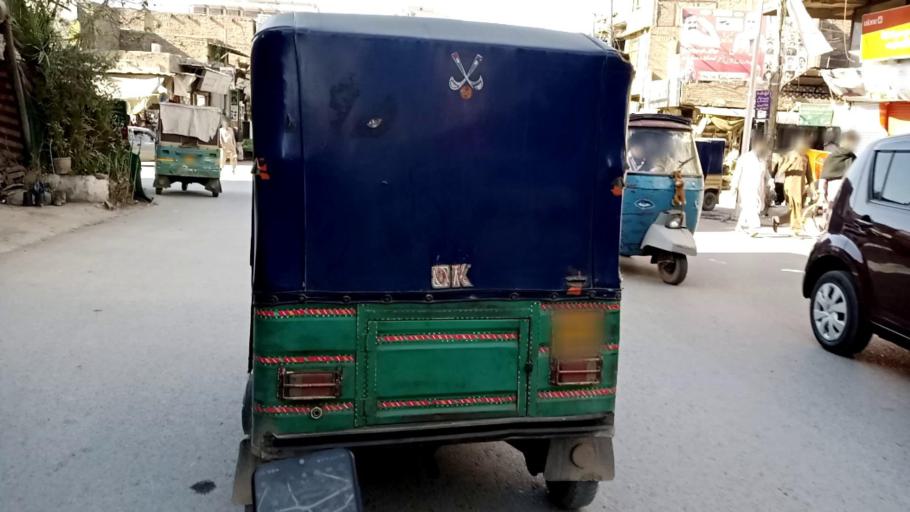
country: PK
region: Khyber Pakhtunkhwa
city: Peshawar
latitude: 34.0071
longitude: 71.5648
